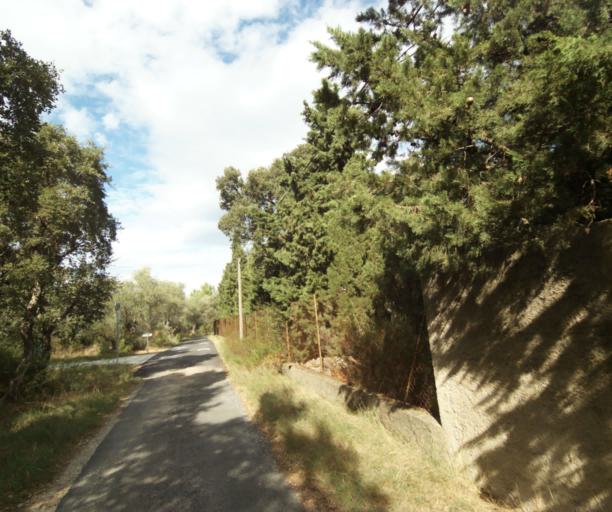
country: FR
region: Languedoc-Roussillon
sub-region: Departement des Pyrenees-Orientales
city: Argelers
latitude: 42.5430
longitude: 2.9973
